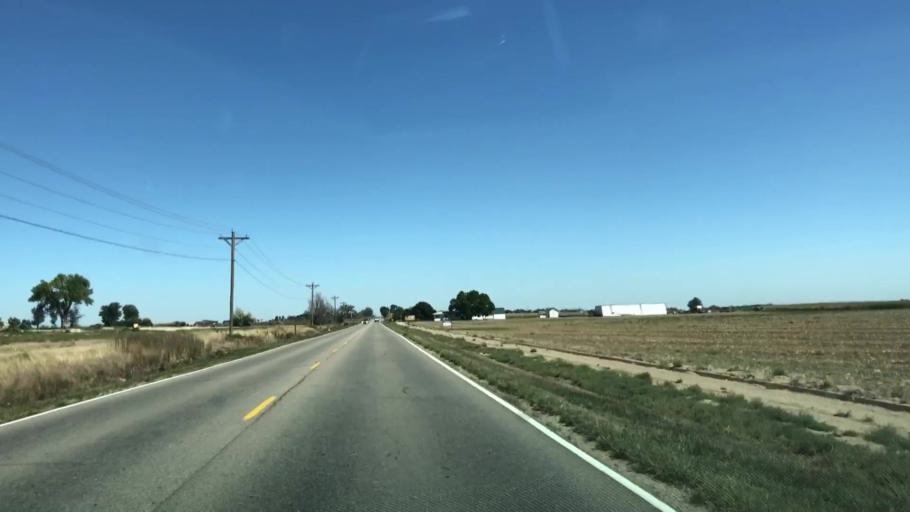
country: US
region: Colorado
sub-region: Weld County
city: Windsor
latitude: 40.5228
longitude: -104.9353
